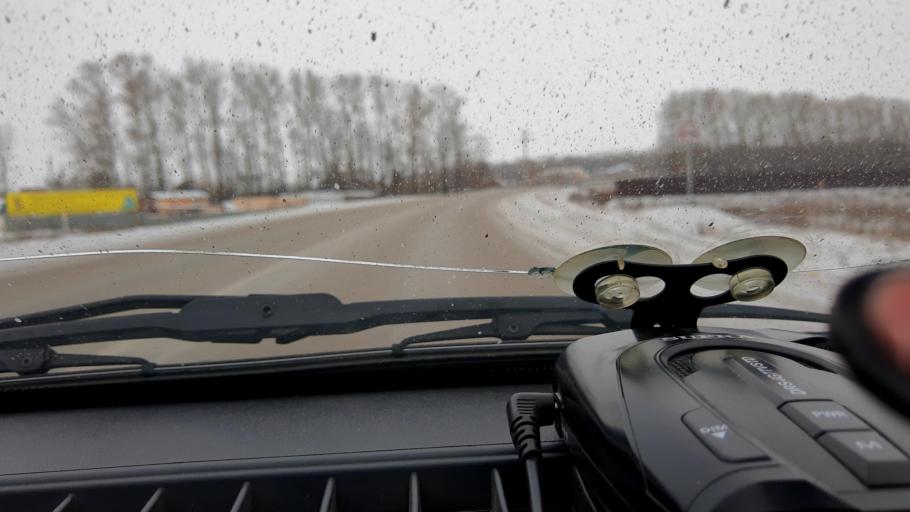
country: RU
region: Bashkortostan
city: Ufa
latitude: 54.6104
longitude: 55.8841
